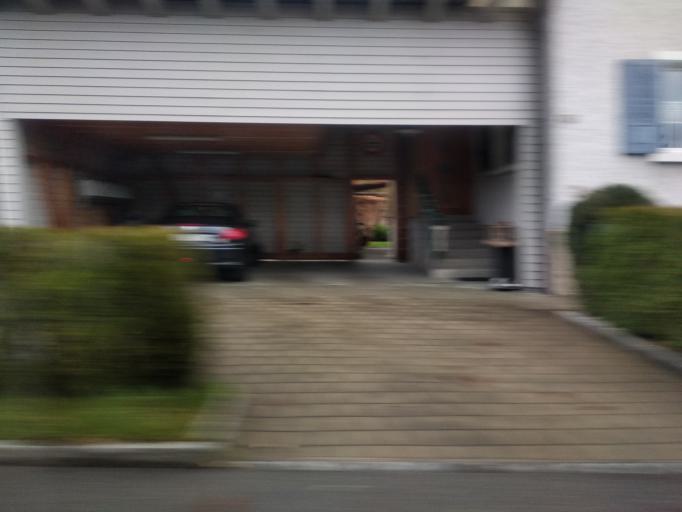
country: CH
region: Saint Gallen
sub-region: Wahlkreis Rheintal
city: Diepoldsau
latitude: 47.3840
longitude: 9.6583
